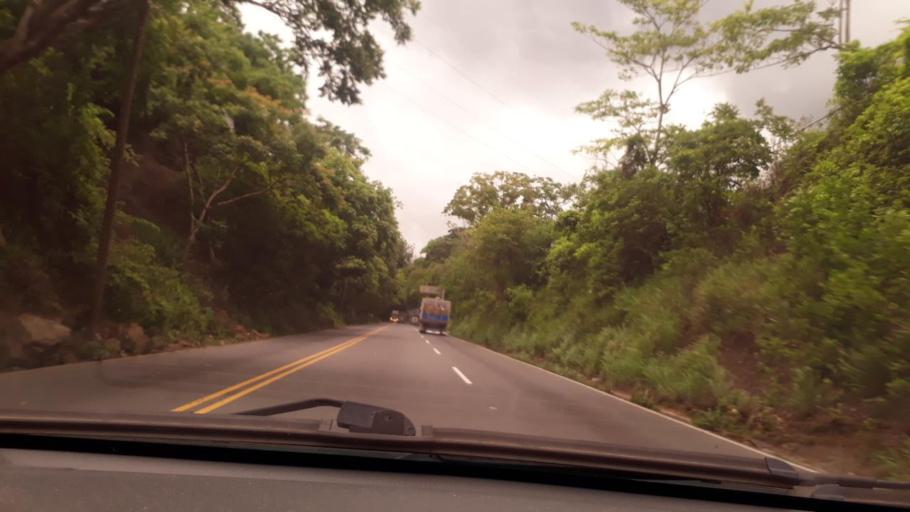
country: GT
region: Izabal
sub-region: Municipio de Los Amates
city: Los Amates
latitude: 15.2265
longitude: -89.2140
